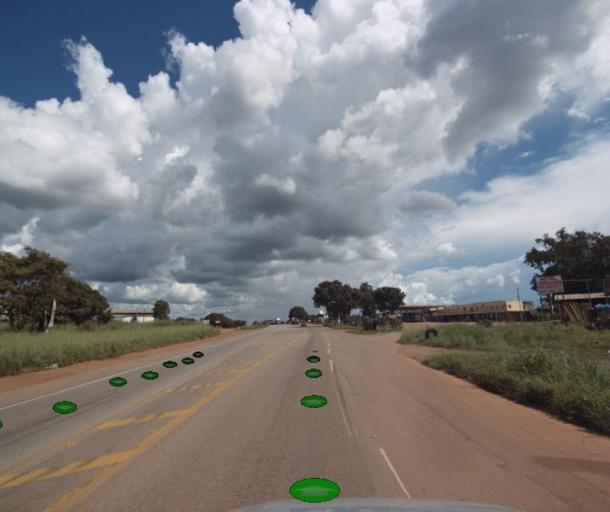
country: BR
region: Goias
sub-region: Porangatu
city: Porangatu
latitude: -13.4504
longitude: -49.1350
